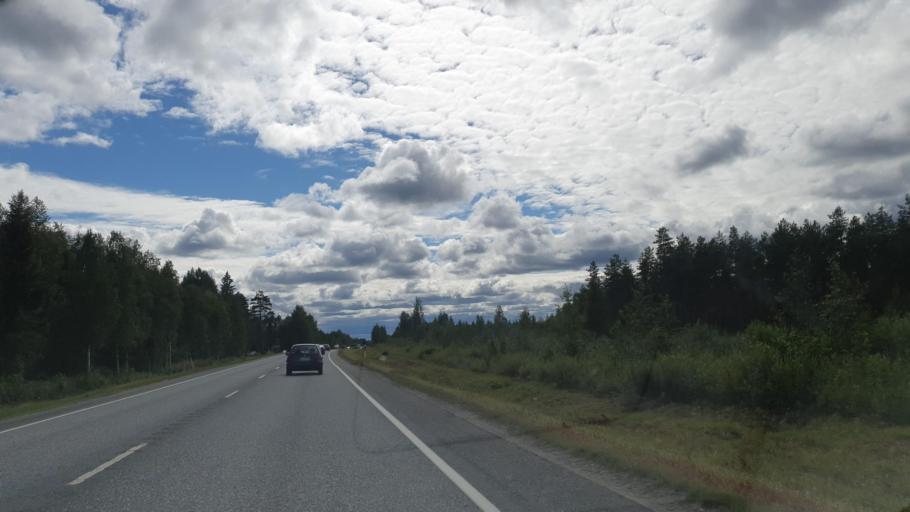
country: FI
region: Kainuu
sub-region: Kajaani
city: Kajaani
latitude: 64.1613
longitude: 27.5230
